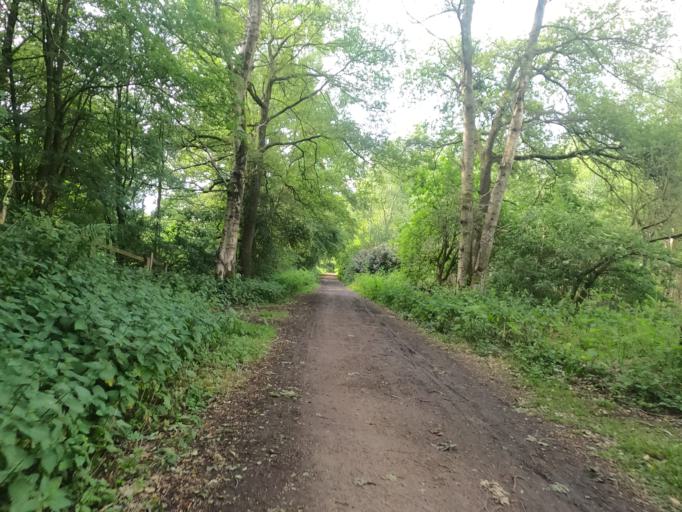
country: GB
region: England
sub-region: Cheshire West and Chester
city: Cuddington
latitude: 53.2233
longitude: -2.6174
